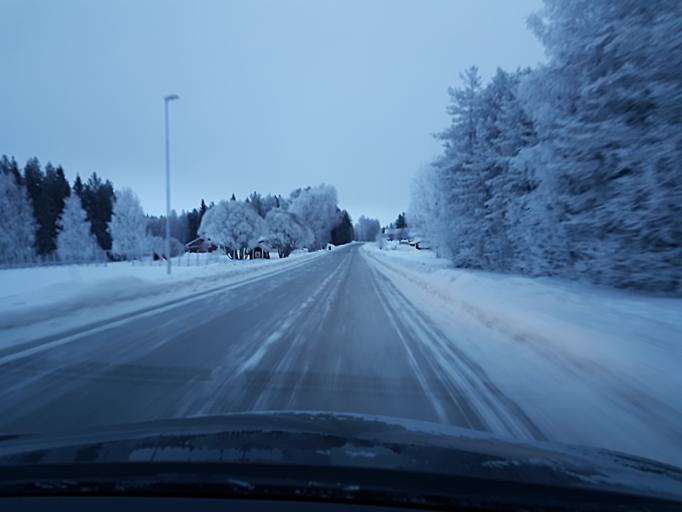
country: SE
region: Norrbotten
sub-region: Pitea Kommun
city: Roknas
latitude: 65.3478
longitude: 21.1127
